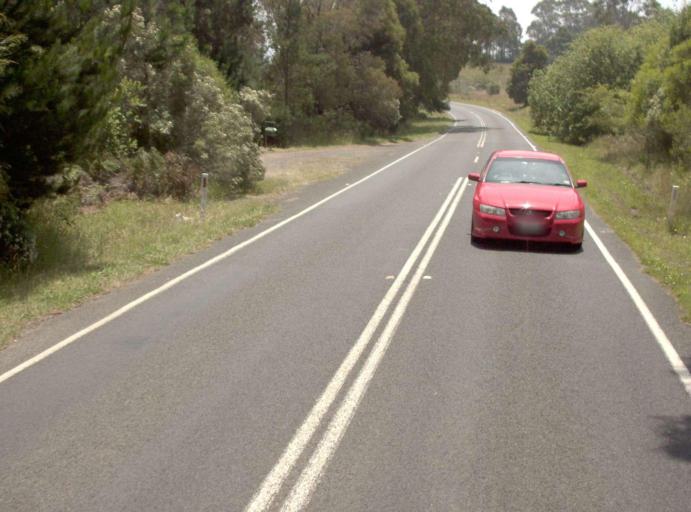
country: AU
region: Victoria
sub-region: Latrobe
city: Traralgon
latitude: -38.3412
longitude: 146.7257
